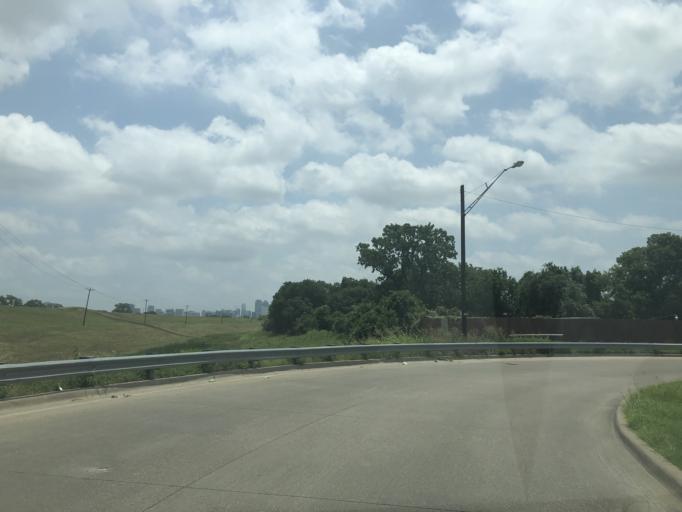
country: US
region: Texas
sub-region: Dallas County
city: Dallas
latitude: 32.7925
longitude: -96.8569
